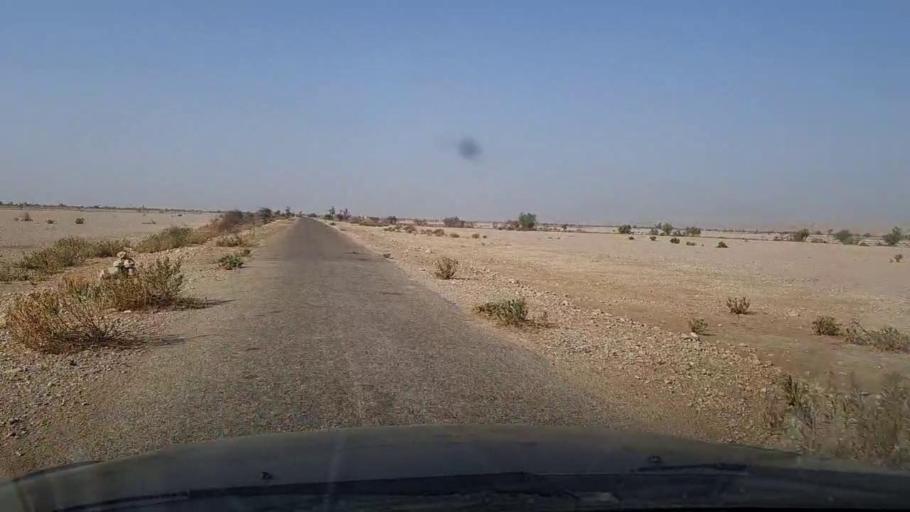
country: PK
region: Sindh
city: Sann
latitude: 25.9097
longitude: 68.0071
